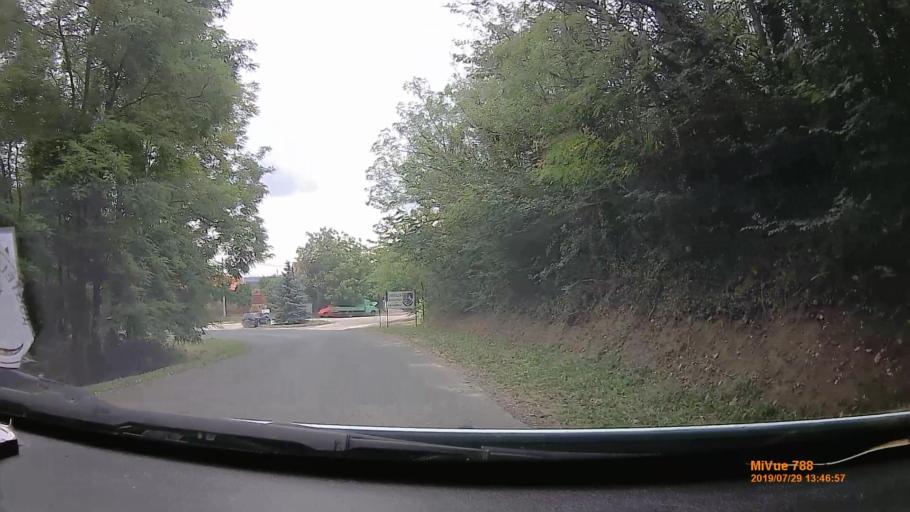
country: HU
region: Somogy
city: Balatonfoldvar
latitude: 46.7845
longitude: 17.9475
